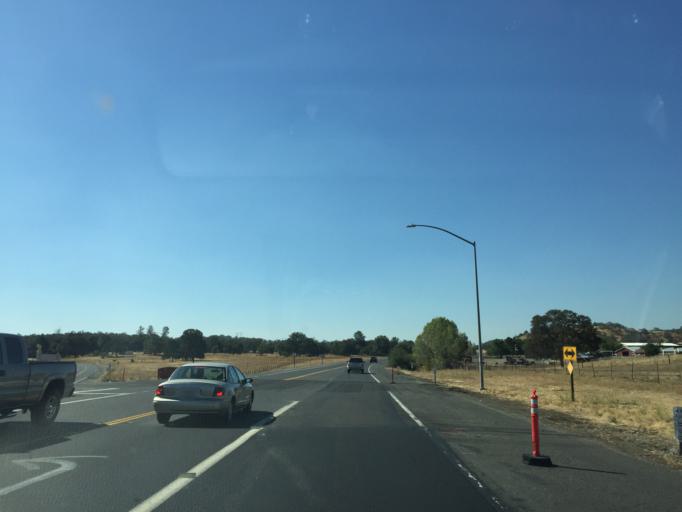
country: US
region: California
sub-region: Tuolumne County
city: Jamestown
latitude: 37.9191
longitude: -120.4516
